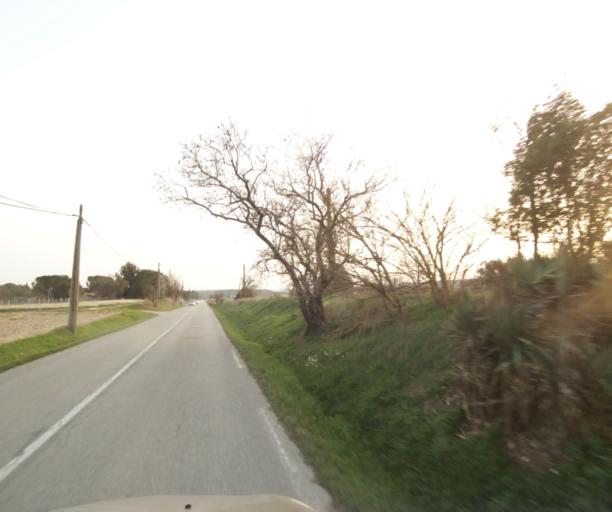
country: FR
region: Provence-Alpes-Cote d'Azur
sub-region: Departement des Bouches-du-Rhone
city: Eguilles
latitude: 43.5519
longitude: 5.3497
